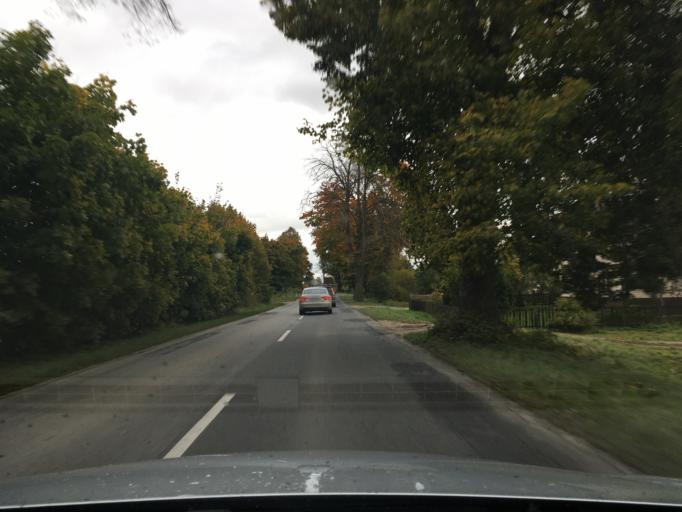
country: PL
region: Pomeranian Voivodeship
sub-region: Powiat koscierski
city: Liniewo
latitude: 54.1343
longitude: 18.2114
